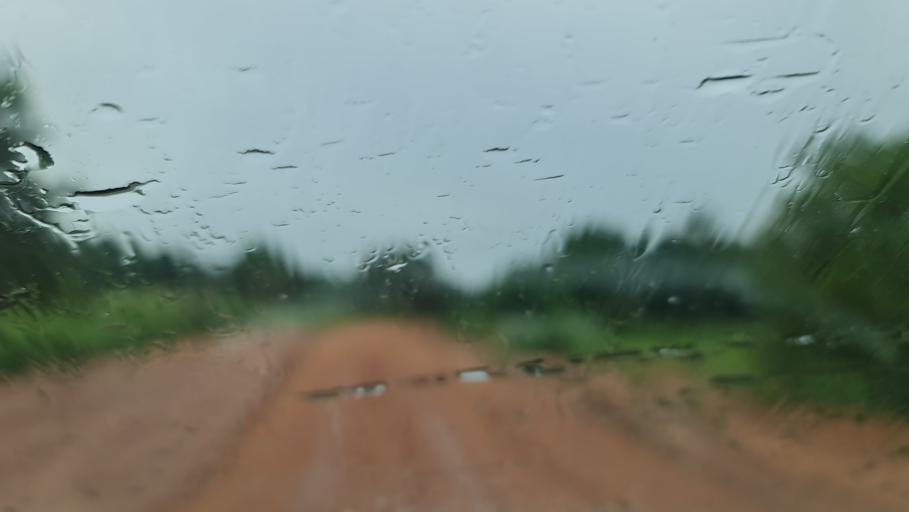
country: MZ
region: Nampula
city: Nacala
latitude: -14.3595
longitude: 40.4603
